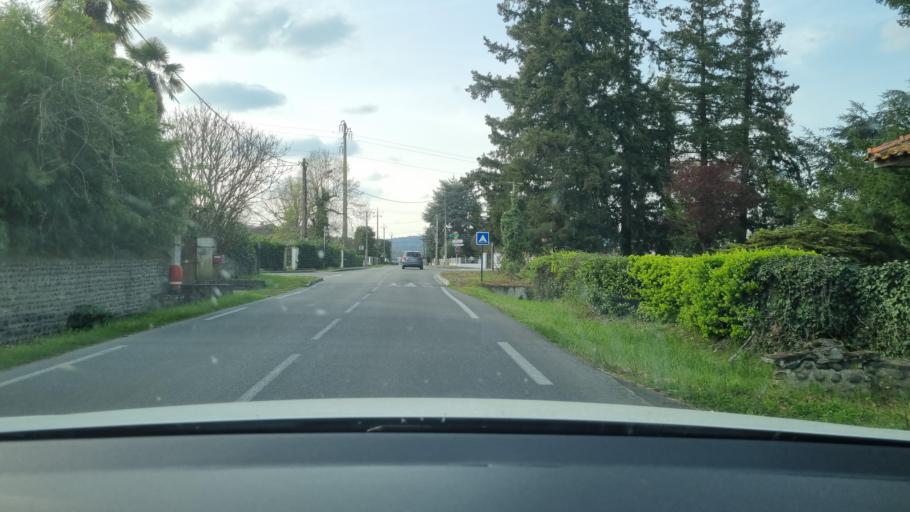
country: FR
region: Midi-Pyrenees
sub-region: Departement des Hautes-Pyrenees
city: Vic-en-Bigorre
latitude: 43.3876
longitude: 0.0399
